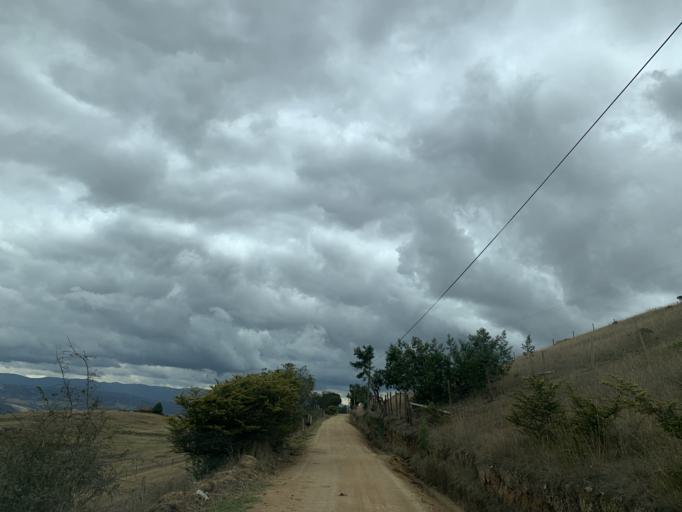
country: CO
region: Boyaca
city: Tunja
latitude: 5.5518
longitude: -73.3175
